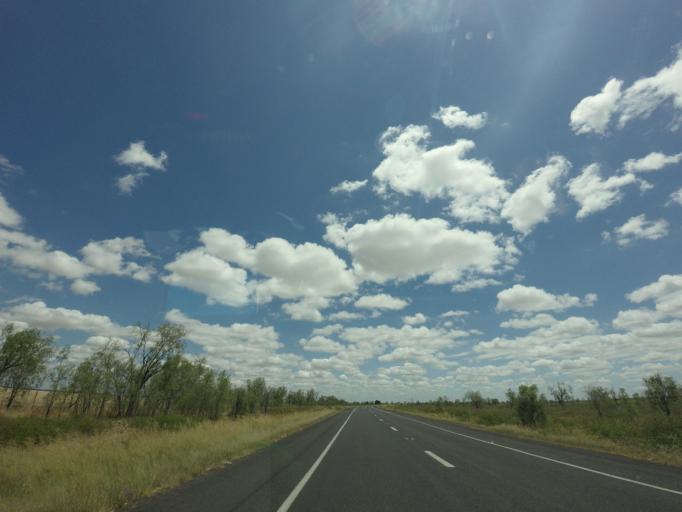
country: AU
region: New South Wales
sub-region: Moree Plains
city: Moree
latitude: -29.0492
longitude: 150.0472
